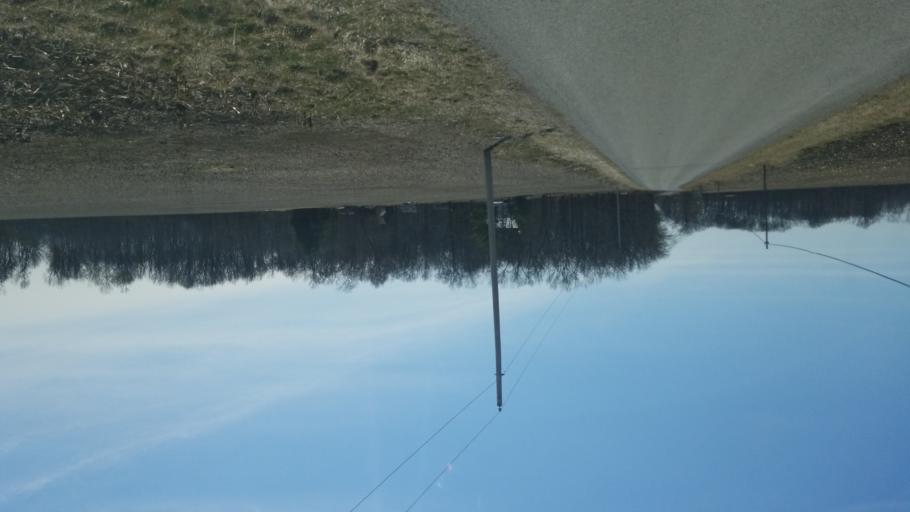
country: US
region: Ohio
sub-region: Crawford County
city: Bucyrus
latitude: 40.6616
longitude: -82.9674
